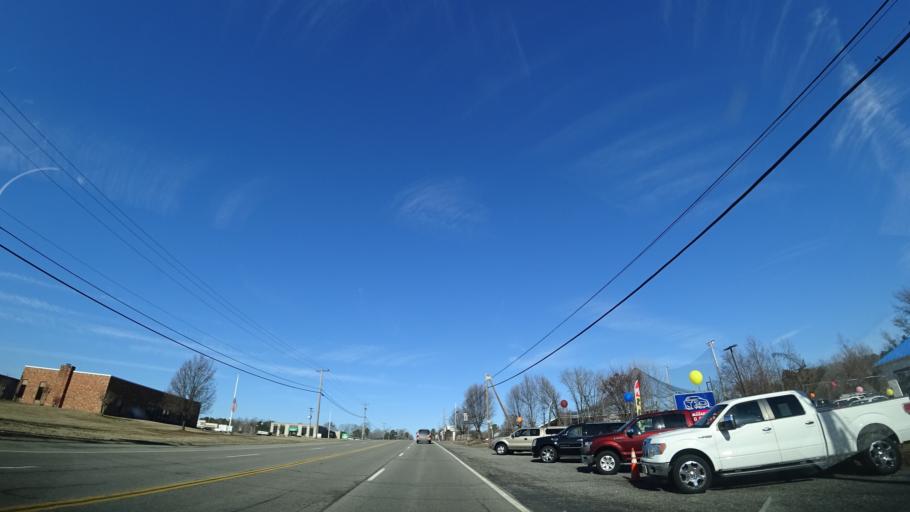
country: US
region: Virginia
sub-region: Henrico County
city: Glen Allen
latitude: 37.6983
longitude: -77.4637
